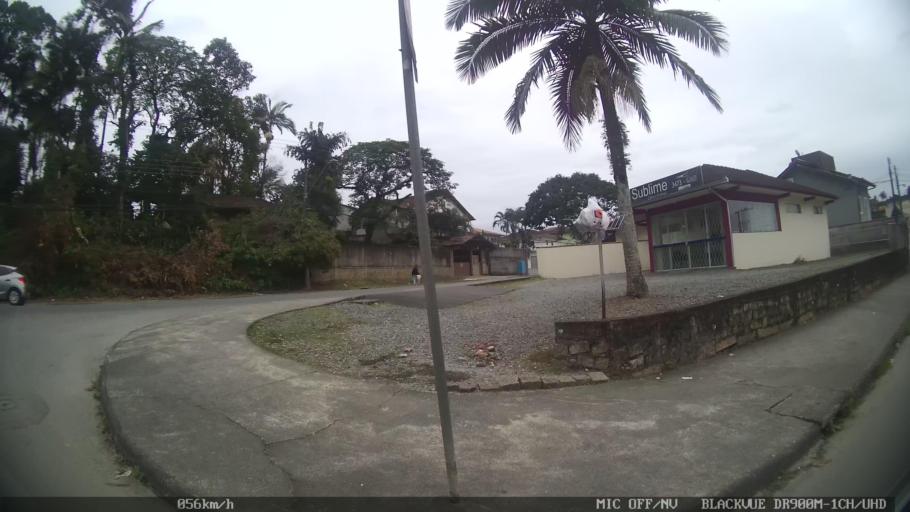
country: BR
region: Santa Catarina
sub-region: Joinville
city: Joinville
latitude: -26.2720
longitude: -48.8866
